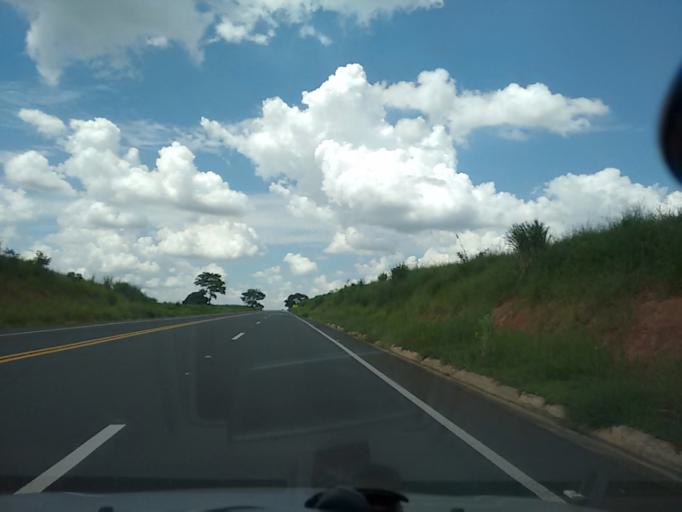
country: BR
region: Sao Paulo
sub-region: Osvaldo Cruz
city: Osvaldo Cruz
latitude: -21.8679
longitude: -50.8525
